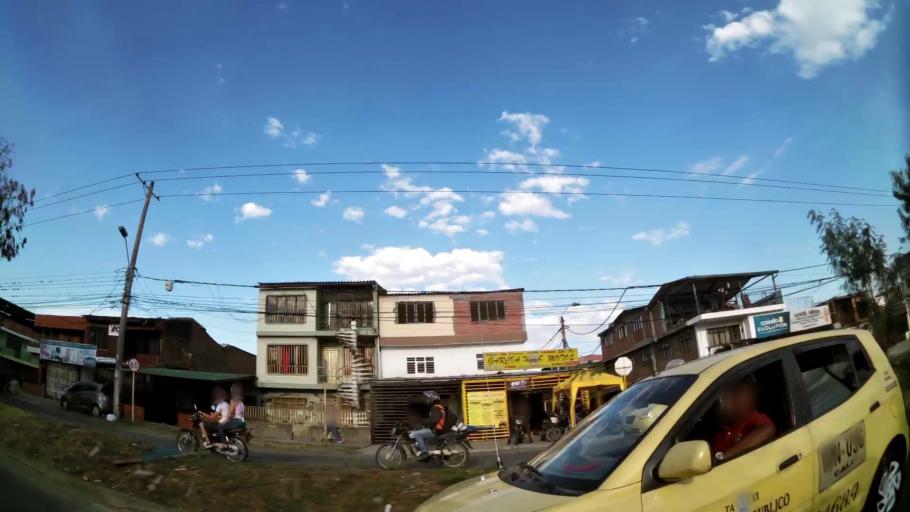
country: CO
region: Valle del Cauca
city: Cali
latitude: 3.4785
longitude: -76.4882
